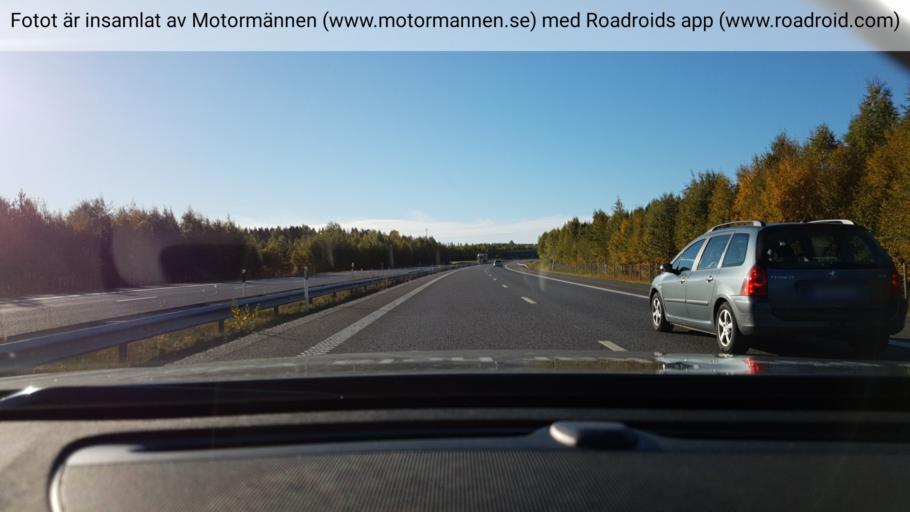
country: SE
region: Norrbotten
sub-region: Pitea Kommun
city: Pitea
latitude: 65.3558
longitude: 21.4357
